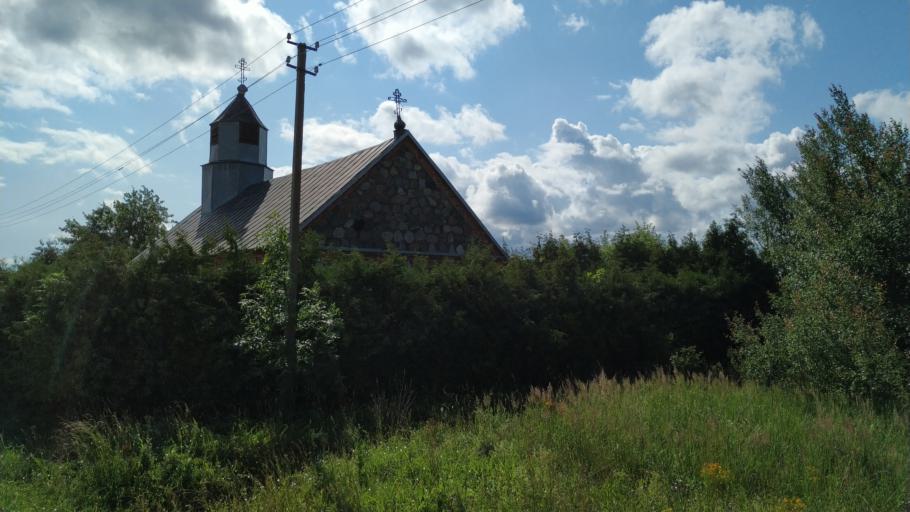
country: LT
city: Kupiskis
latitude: 55.9043
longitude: 25.0298
